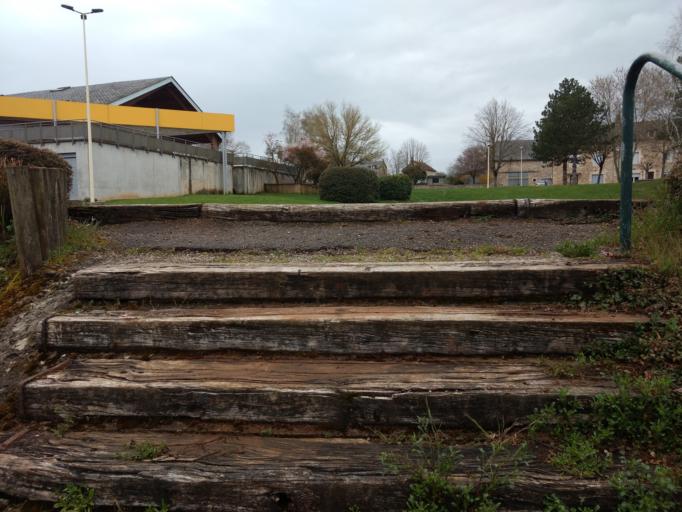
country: FR
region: Midi-Pyrenees
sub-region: Departement de l'Aveyron
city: La Loubiere
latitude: 44.3976
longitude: 2.7049
